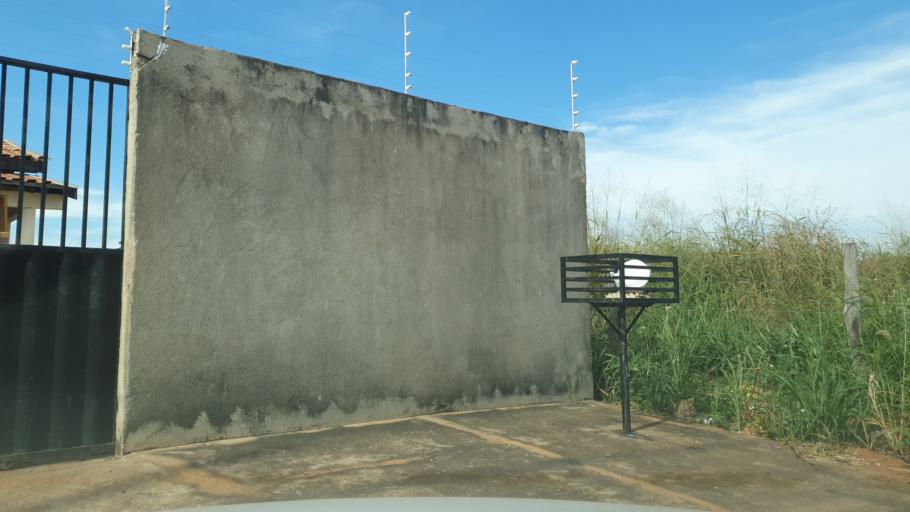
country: BR
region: Mato Grosso
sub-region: Pontes E Lacerda
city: Pontes e Lacerda
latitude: -15.2499
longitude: -59.3204
